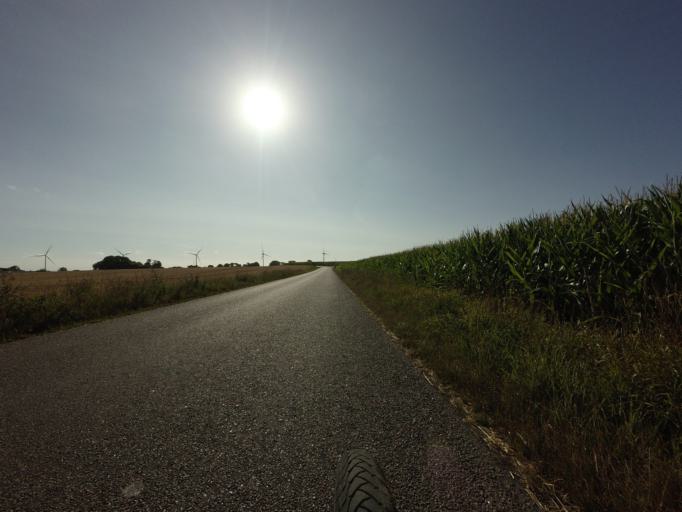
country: DK
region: North Denmark
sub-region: Hjorring Kommune
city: Vra
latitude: 57.3801
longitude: 10.0045
